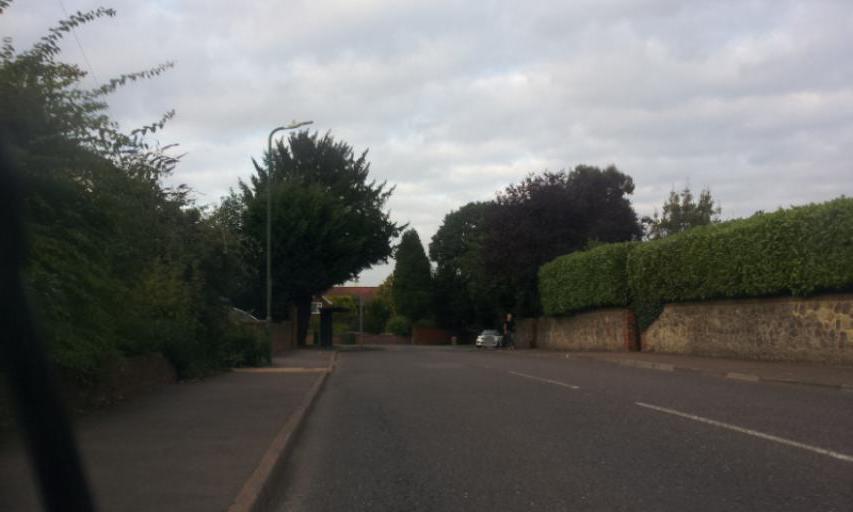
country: GB
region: England
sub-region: Kent
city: Maidstone
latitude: 51.2747
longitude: 0.5001
